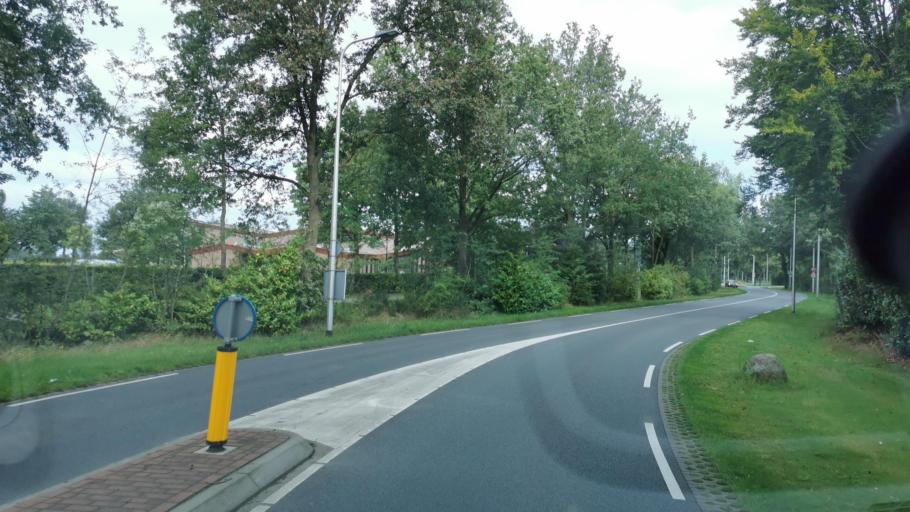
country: NL
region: Overijssel
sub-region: Gemeente Oldenzaal
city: Oldenzaal
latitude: 52.3118
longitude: 6.8941
